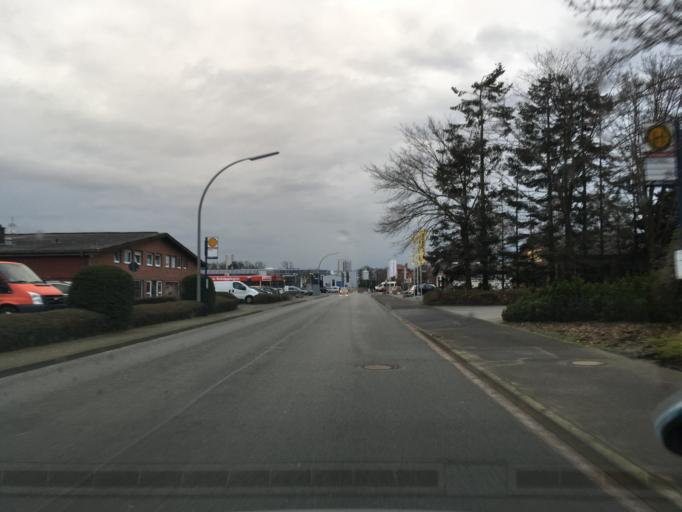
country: DE
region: North Rhine-Westphalia
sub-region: Regierungsbezirk Munster
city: Schoppingen
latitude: 52.0865
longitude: 7.2325
